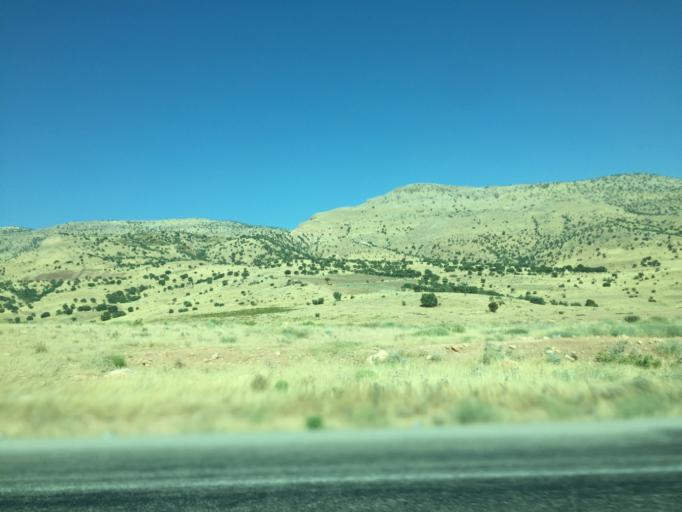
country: TR
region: Batman
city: Hasankeyf
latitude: 37.6649
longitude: 41.4521
